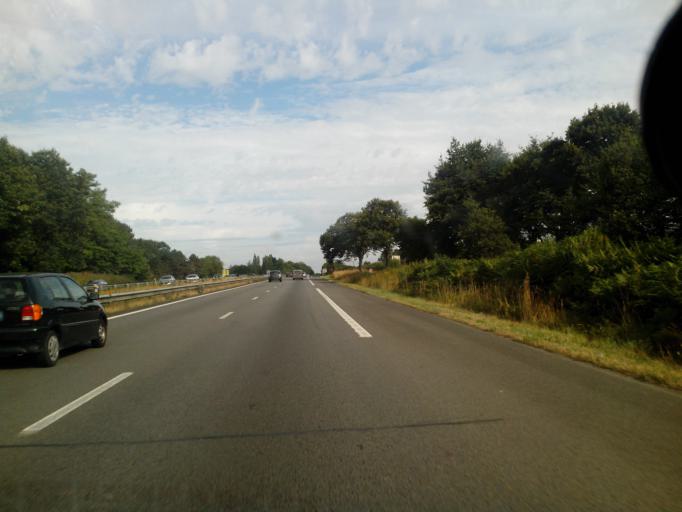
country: FR
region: Pays de la Loire
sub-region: Departement de la Loire-Atlantique
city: Vigneux-de-Bretagne
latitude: 47.2817
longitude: -1.7285
